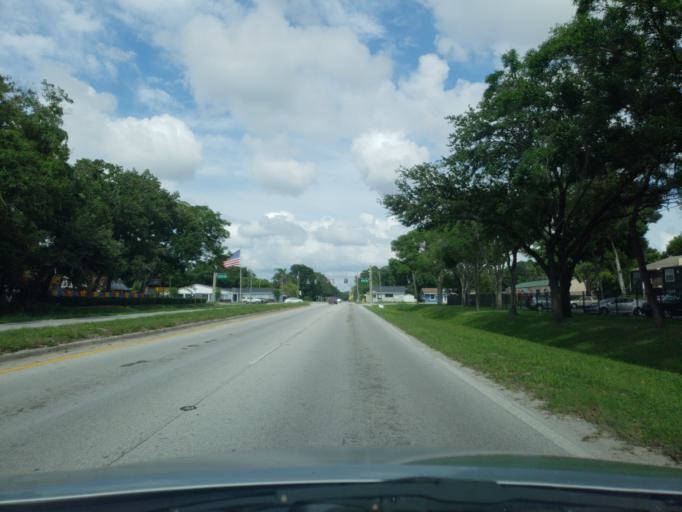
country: US
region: Florida
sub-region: Hillsborough County
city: Egypt Lake-Leto
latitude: 28.0071
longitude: -82.5022
